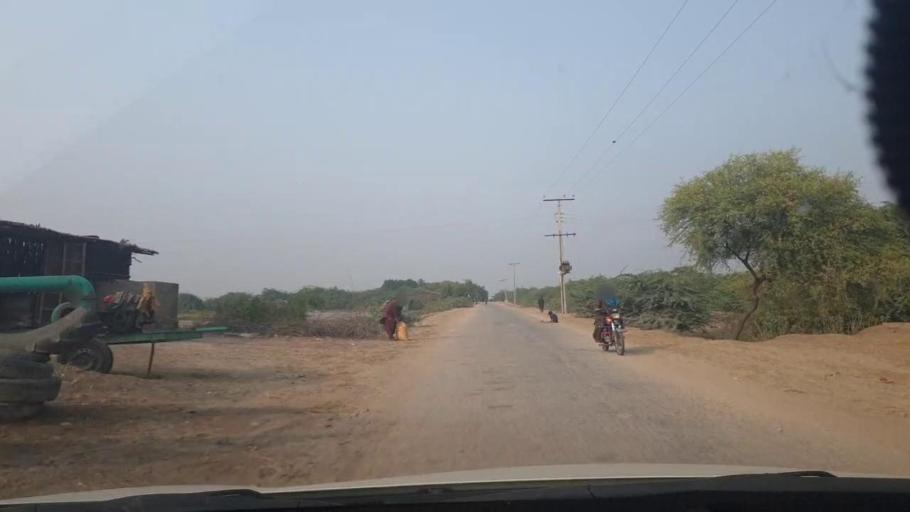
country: PK
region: Sindh
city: Bulri
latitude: 24.7625
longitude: 68.4200
